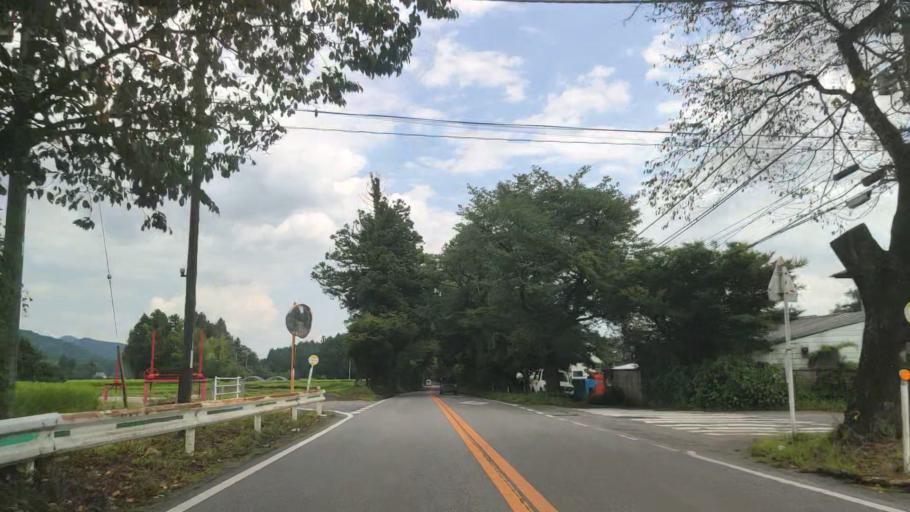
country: JP
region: Tochigi
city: Imaichi
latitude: 36.6888
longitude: 139.7698
